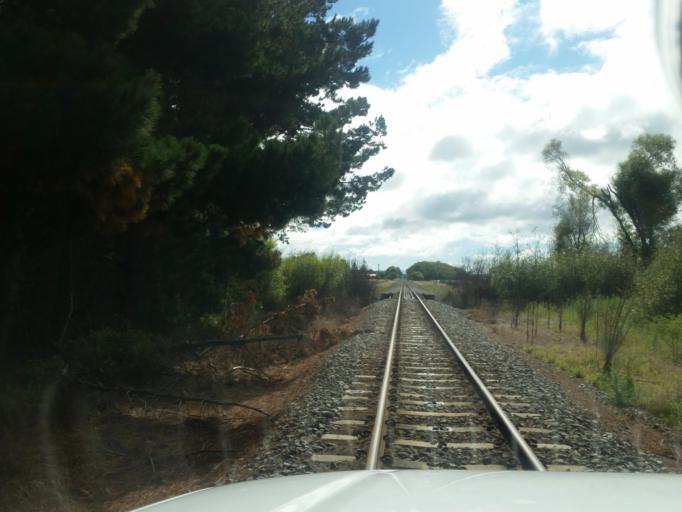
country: NZ
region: Canterbury
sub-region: Waimakariri District
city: Kaiapoi
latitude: -43.4015
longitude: 172.6520
